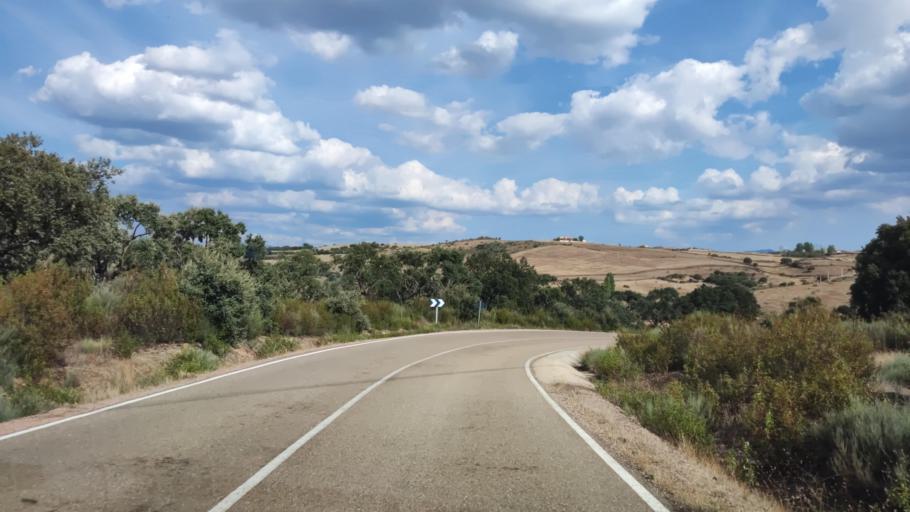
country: ES
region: Castille and Leon
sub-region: Provincia de Salamanca
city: Pastores
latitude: 40.5219
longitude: -6.5181
